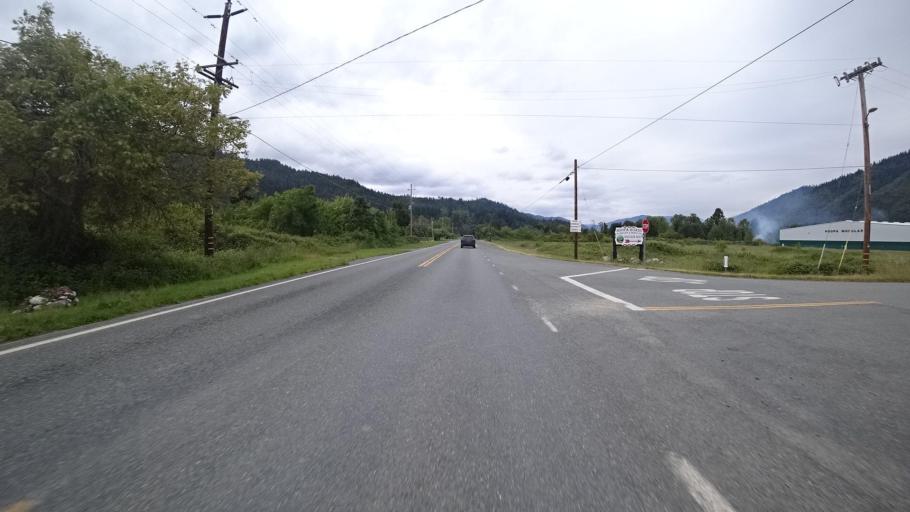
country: US
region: California
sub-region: Humboldt County
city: Willow Creek
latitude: 41.0283
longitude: -123.6592
